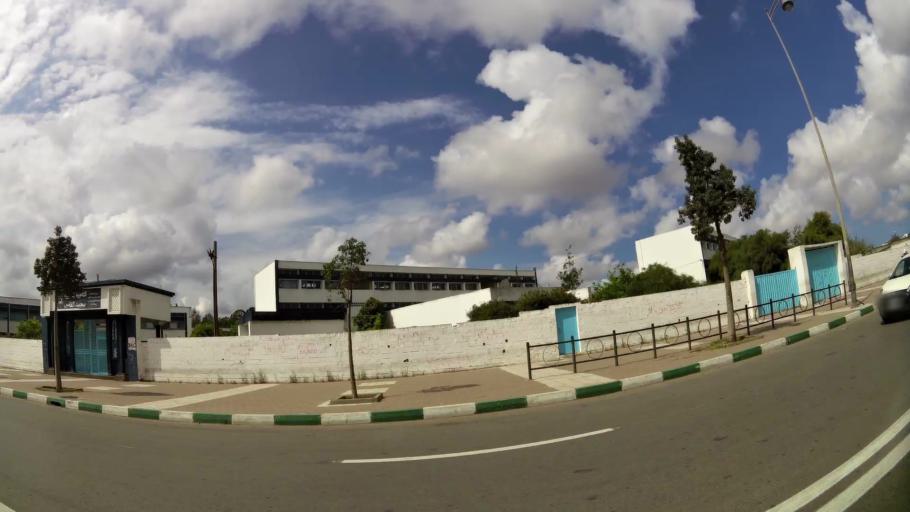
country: MA
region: Gharb-Chrarda-Beni Hssen
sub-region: Kenitra Province
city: Kenitra
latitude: 34.2586
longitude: -6.5641
